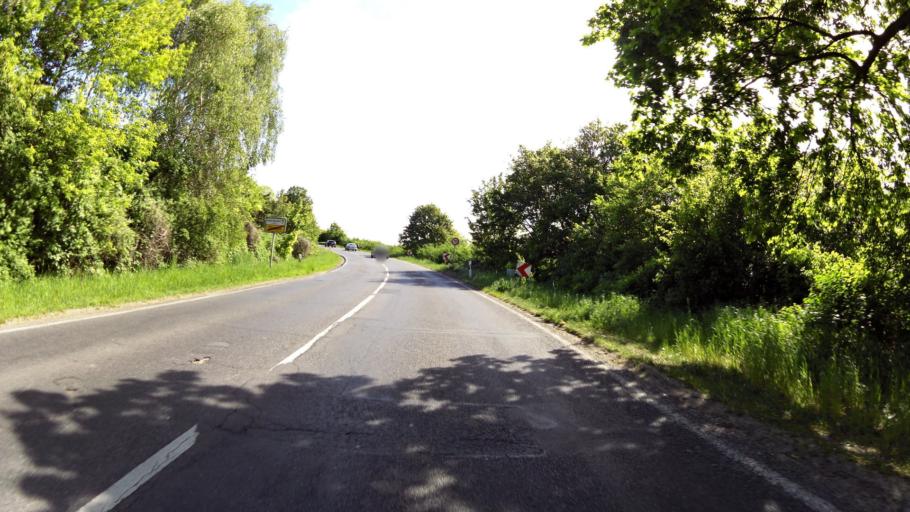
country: DE
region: Brandenburg
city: Hohen Neuendorf
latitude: 52.6575
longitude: 13.2577
